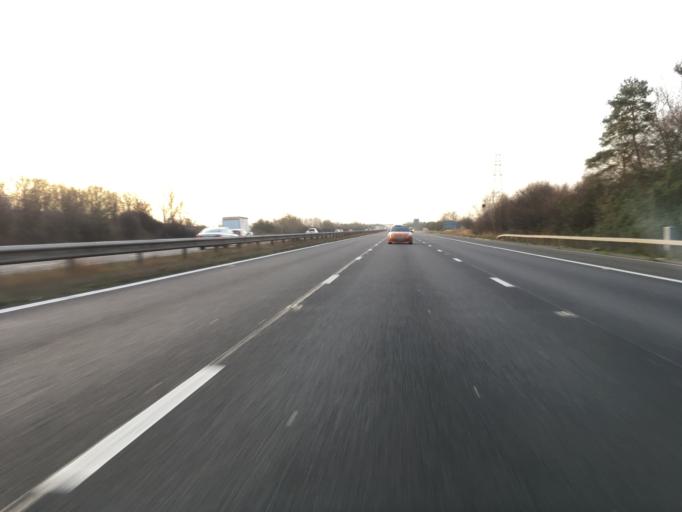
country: GB
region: England
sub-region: Worcestershire
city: Bredon
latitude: 51.9949
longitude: -2.1240
